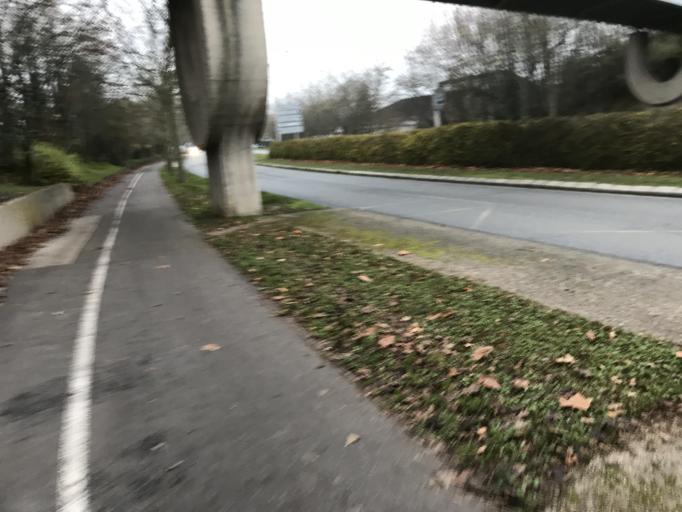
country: FR
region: Ile-de-France
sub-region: Departement des Yvelines
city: Montigny-le-Bretonneux
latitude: 48.7622
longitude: 2.0381
